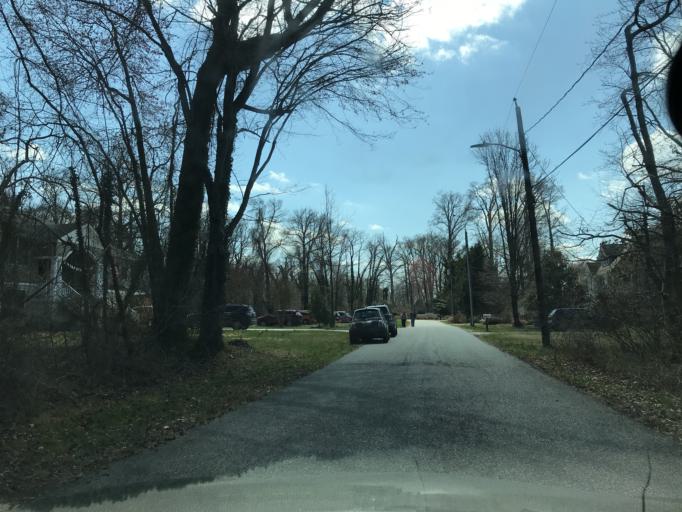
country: US
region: Maryland
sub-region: Harford County
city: Riverside
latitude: 39.4479
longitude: -76.2330
